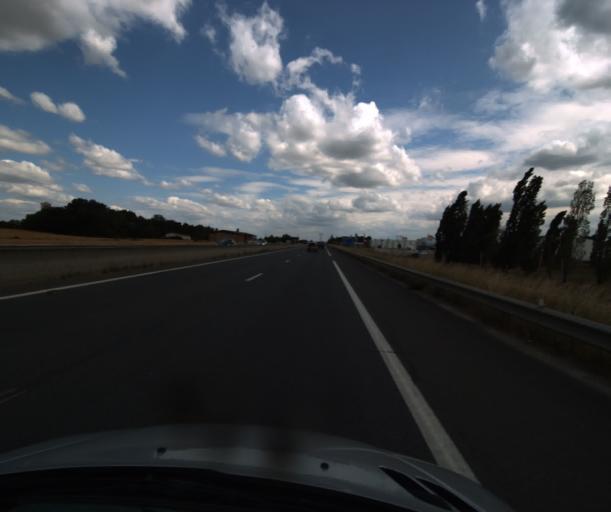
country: FR
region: Midi-Pyrenees
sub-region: Departement du Tarn-et-Garonne
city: Bressols
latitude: 43.9454
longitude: 1.3235
